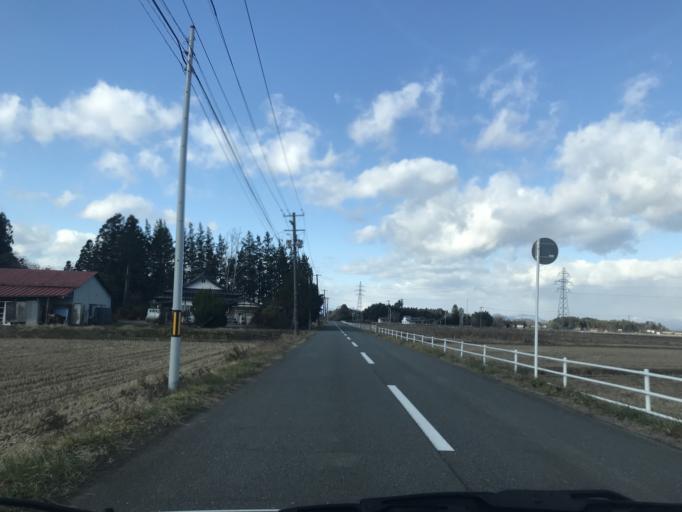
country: JP
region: Miyagi
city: Kogota
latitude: 38.7392
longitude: 141.0529
